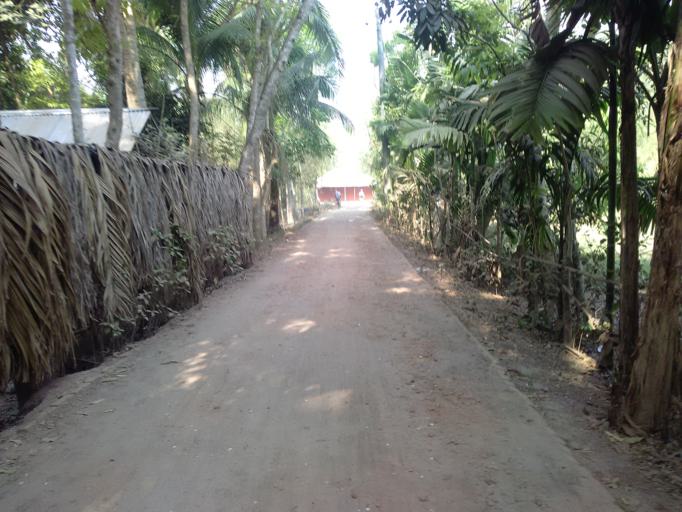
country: BD
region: Khulna
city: Khulna
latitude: 22.8972
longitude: 89.5286
